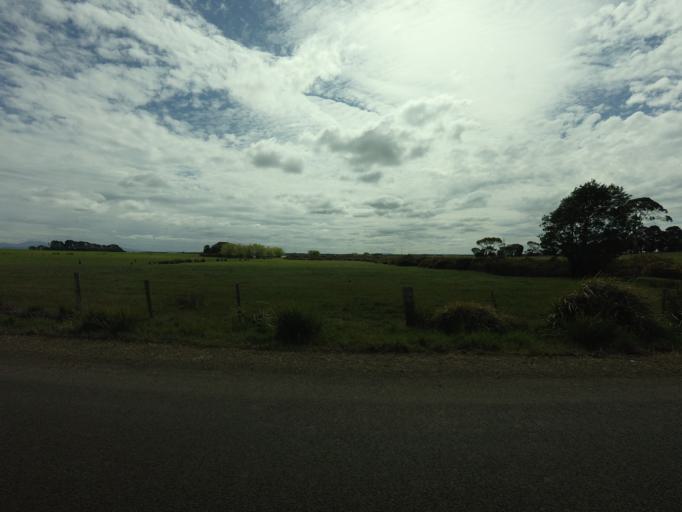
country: AU
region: Tasmania
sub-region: Northern Midlands
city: Longford
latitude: -41.7150
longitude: 147.1910
